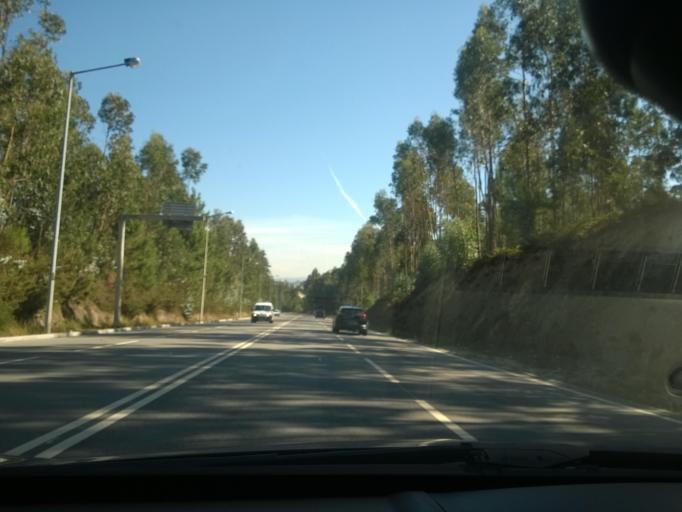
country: PT
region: Porto
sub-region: Maia
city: Anta
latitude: 41.2570
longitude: -8.6307
